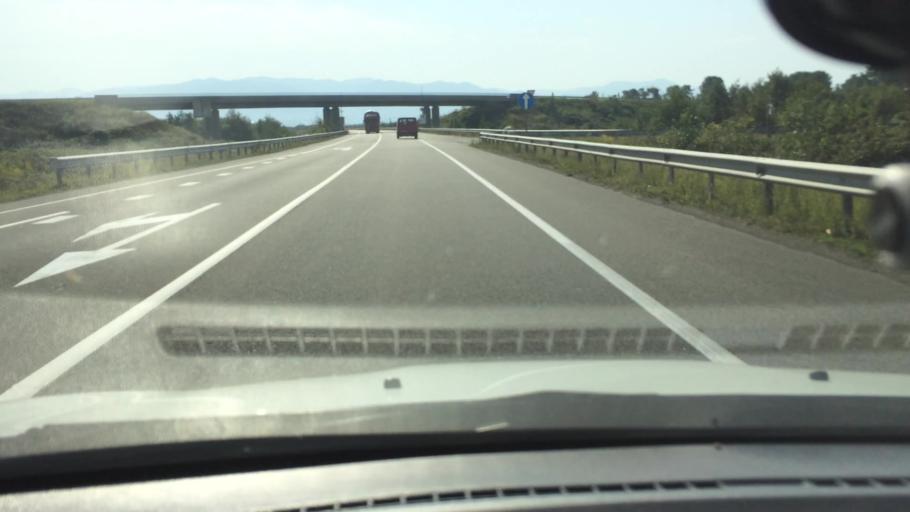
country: GE
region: Guria
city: Urek'i
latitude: 41.9192
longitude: 41.7753
